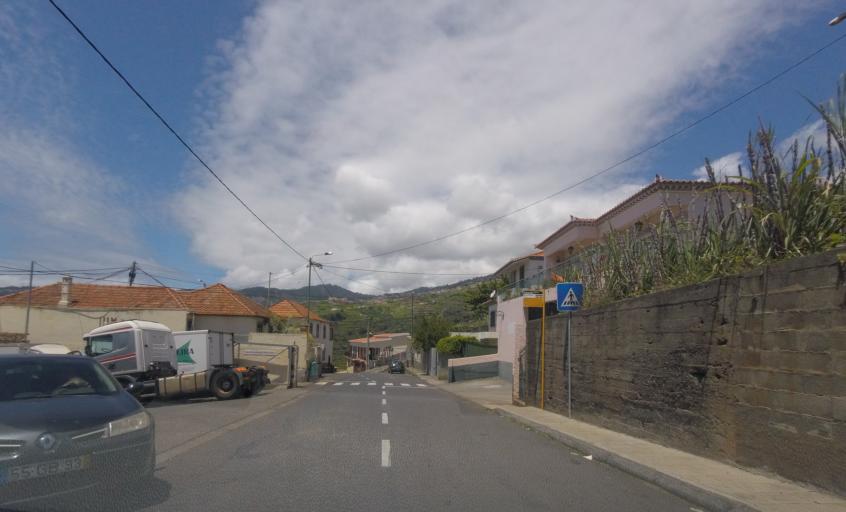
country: PT
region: Madeira
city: Camara de Lobos
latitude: 32.6629
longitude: -16.9542
